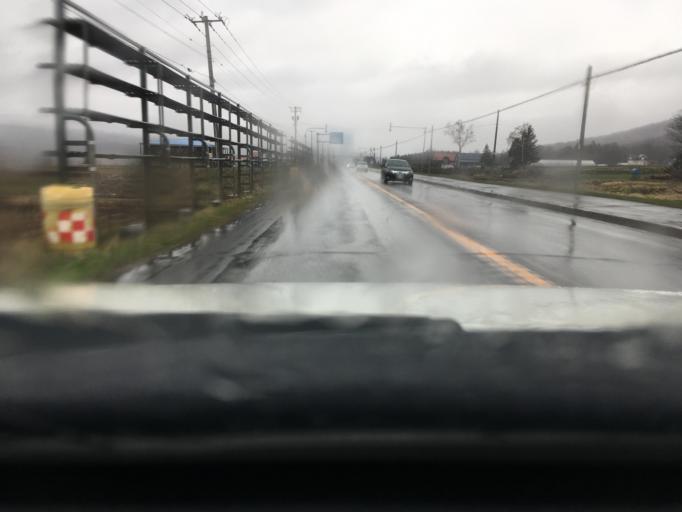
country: JP
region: Hokkaido
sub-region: Asahikawa-shi
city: Asahikawa
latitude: 43.9154
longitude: 142.4879
